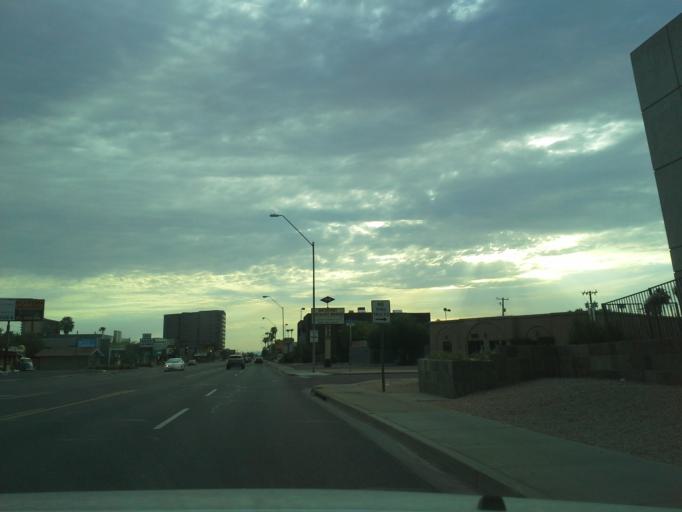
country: US
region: Arizona
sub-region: Maricopa County
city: Phoenix
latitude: 33.5093
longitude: -112.0660
